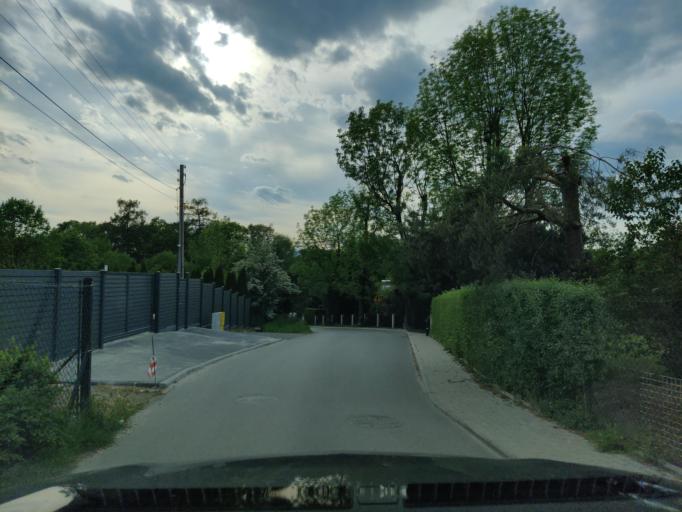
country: PL
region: Silesian Voivodeship
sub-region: Powiat zywiecki
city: Zywiec
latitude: 49.7105
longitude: 19.2084
